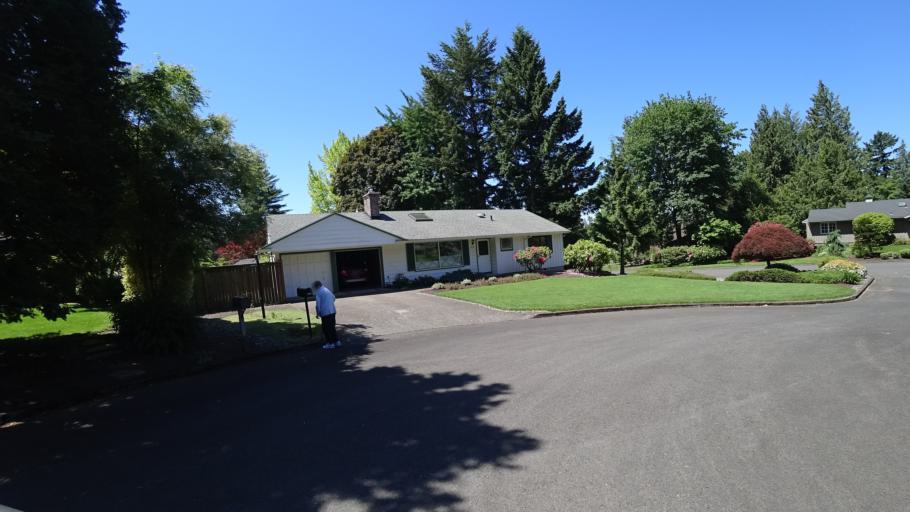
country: US
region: Oregon
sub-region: Washington County
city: Raleigh Hills
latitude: 45.4886
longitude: -122.7174
